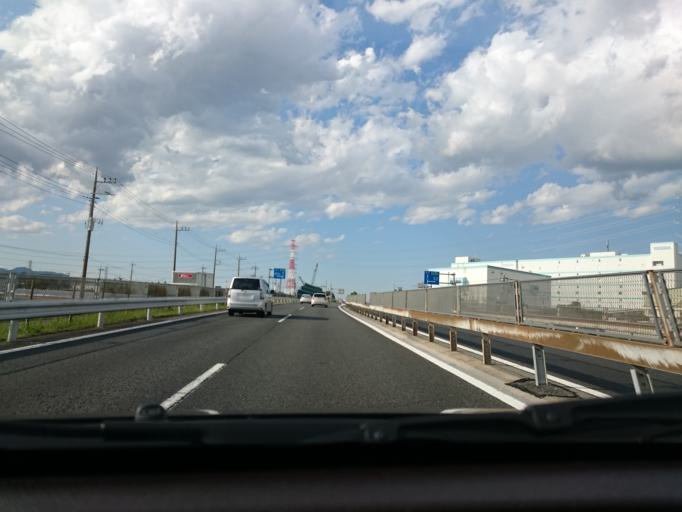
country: JP
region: Kanagawa
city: Isehara
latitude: 35.4013
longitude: 139.3351
